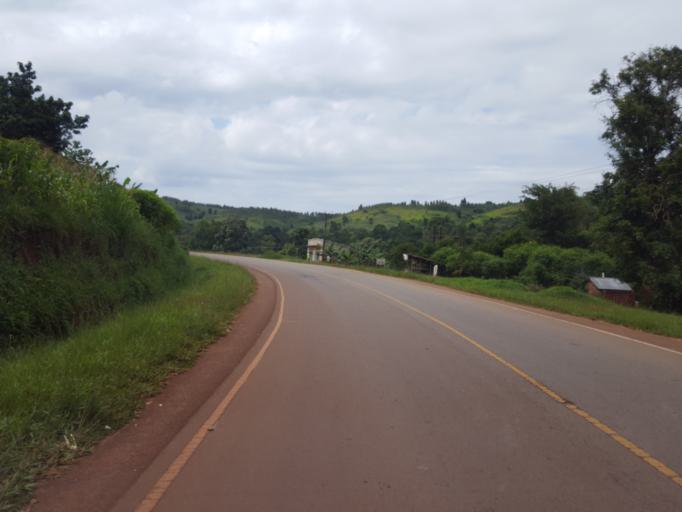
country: UG
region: Central Region
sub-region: Mityana District
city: Mityana
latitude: 0.6283
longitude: 32.1165
